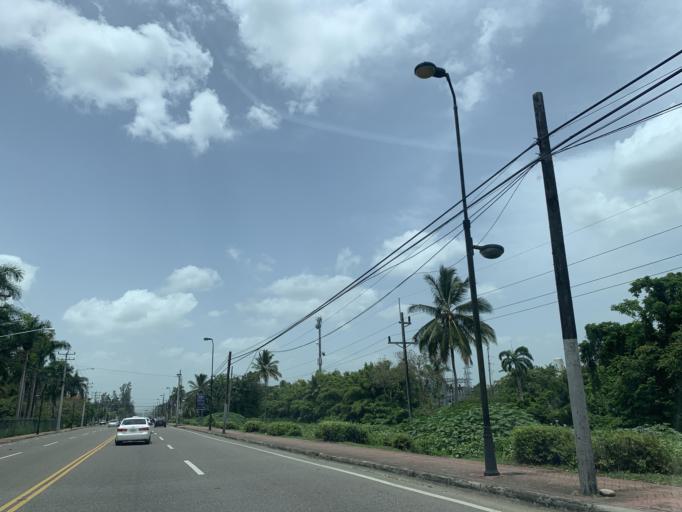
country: DO
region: Puerto Plata
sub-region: Puerto Plata
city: Puerto Plata
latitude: 19.7695
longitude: -70.6528
